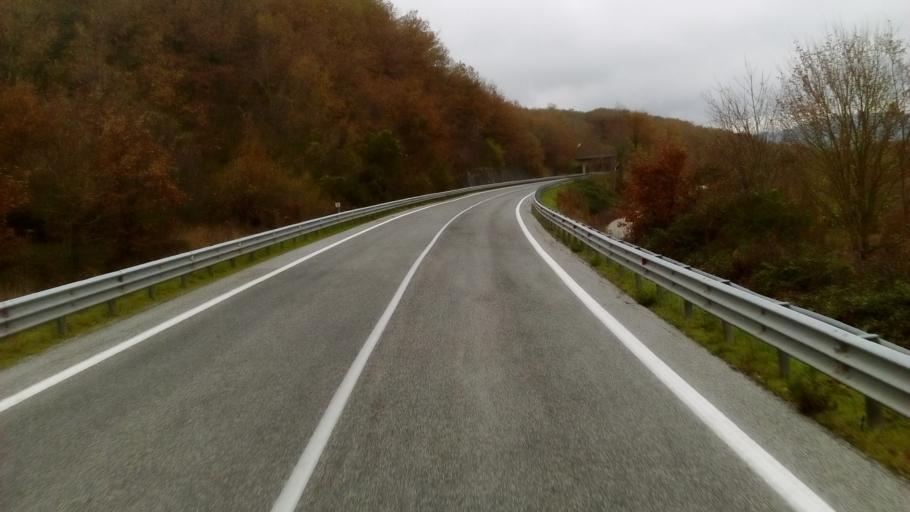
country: IT
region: Molise
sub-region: Provincia di Isernia
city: Chiauci
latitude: 41.6719
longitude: 14.3636
